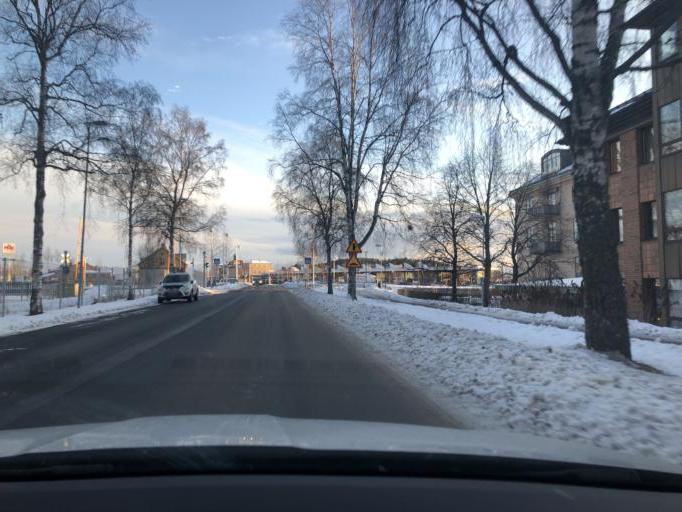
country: SE
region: Dalarna
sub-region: Faluns Kommun
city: Falun
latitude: 60.6061
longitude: 15.6387
